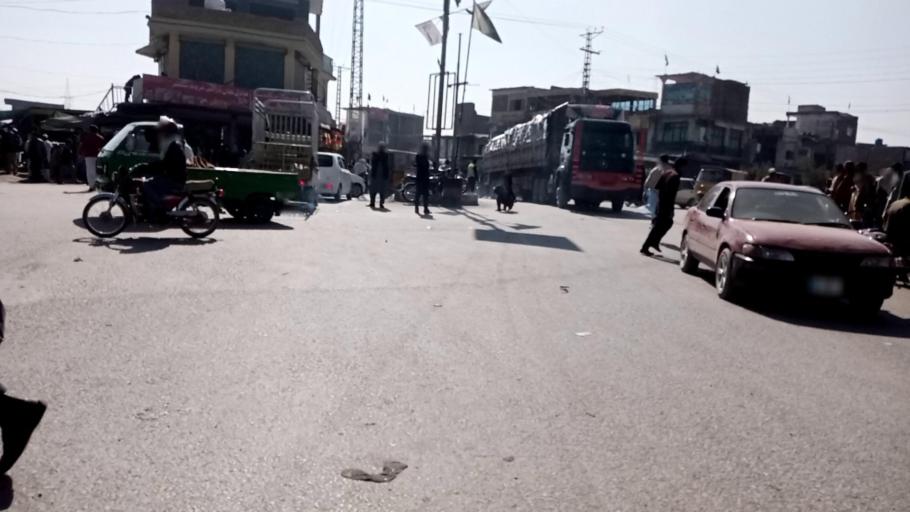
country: PK
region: Khyber Pakhtunkhwa
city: Peshawar
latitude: 33.9156
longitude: 71.4603
